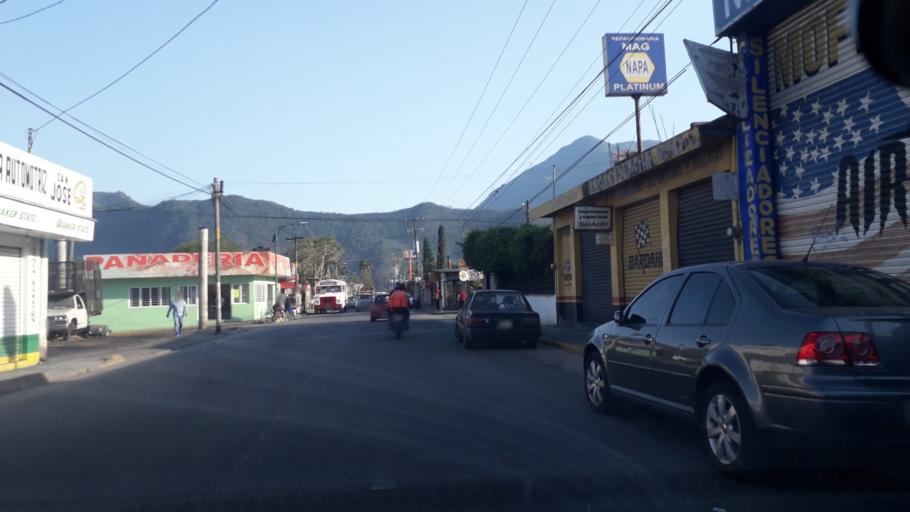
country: MX
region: Veracruz
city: Jalapilla
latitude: 18.8267
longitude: -97.0901
